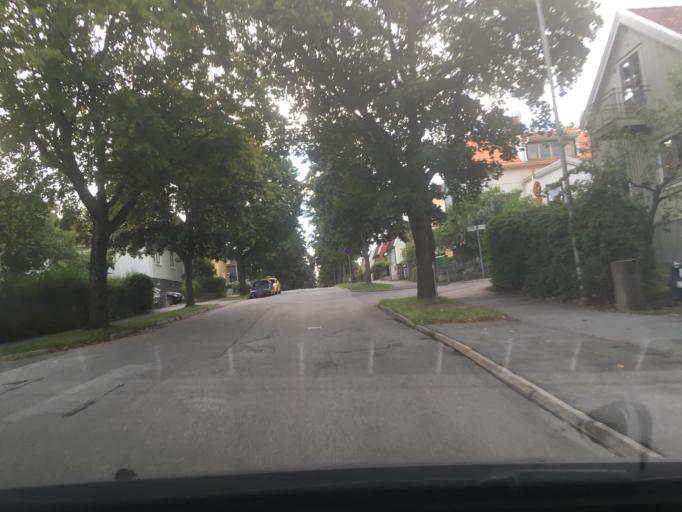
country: SE
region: Stockholm
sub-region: Stockholms Kommun
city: Bromma
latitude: 59.3320
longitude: 17.9355
